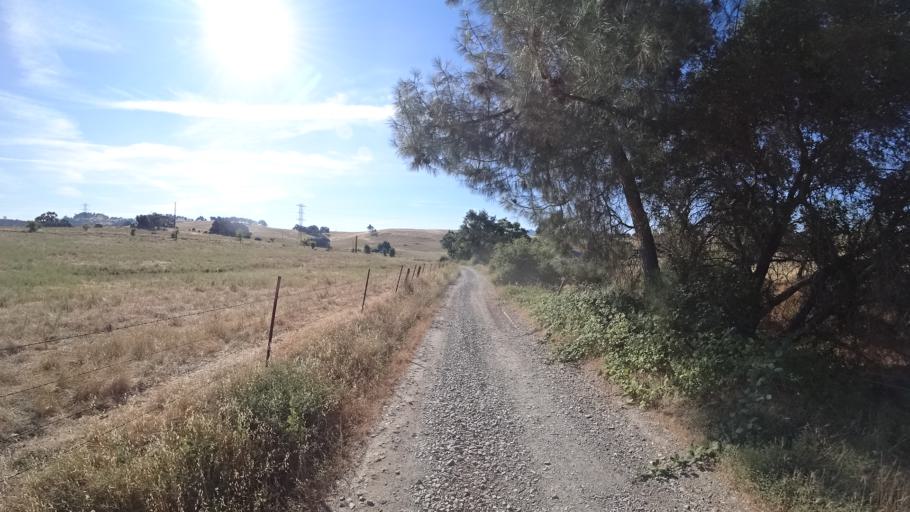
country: US
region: California
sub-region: Calaveras County
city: Valley Springs
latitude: 38.2221
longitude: -120.7869
